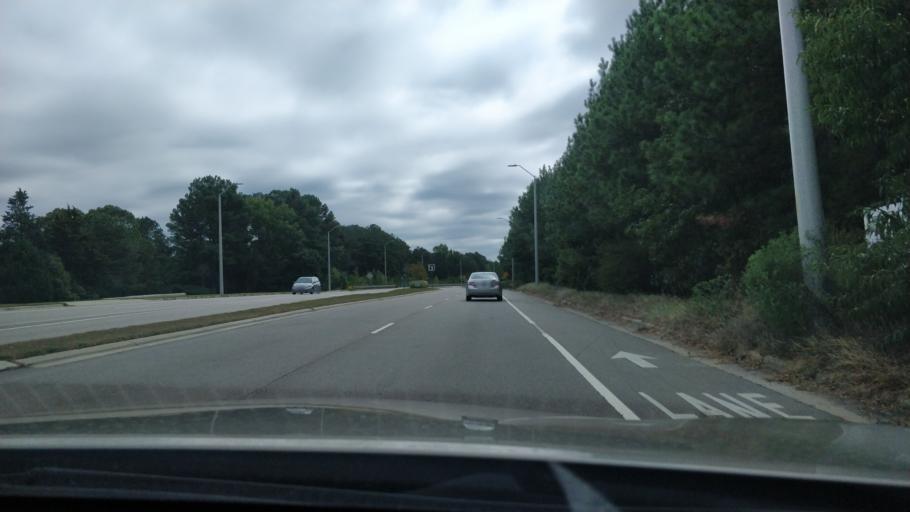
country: US
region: North Carolina
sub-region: Wake County
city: Morrisville
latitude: 35.9162
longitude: -78.7297
